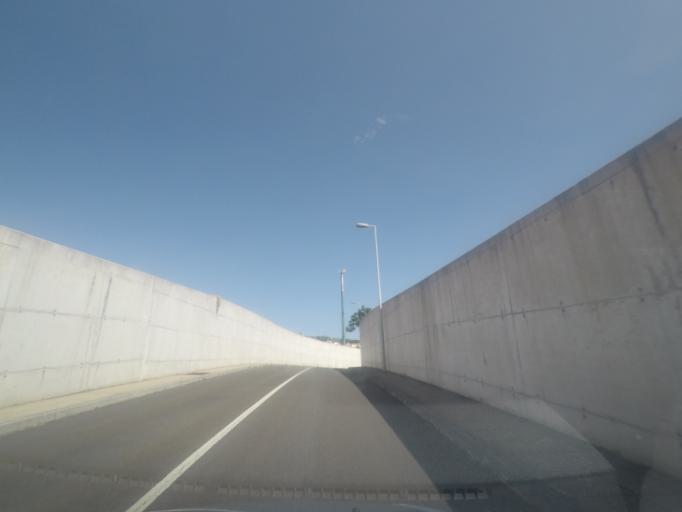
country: PT
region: Madeira
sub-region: Calheta
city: Faja da Ovelha
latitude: 32.8149
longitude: -17.2524
